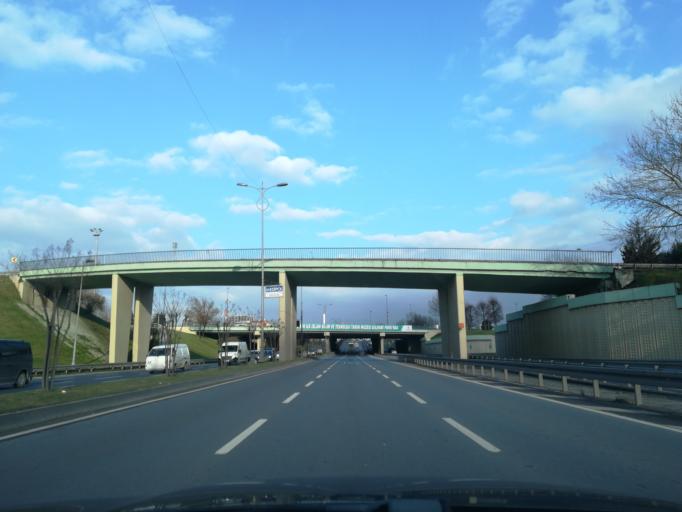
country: TR
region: Istanbul
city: Istanbul
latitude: 41.0274
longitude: 28.9257
